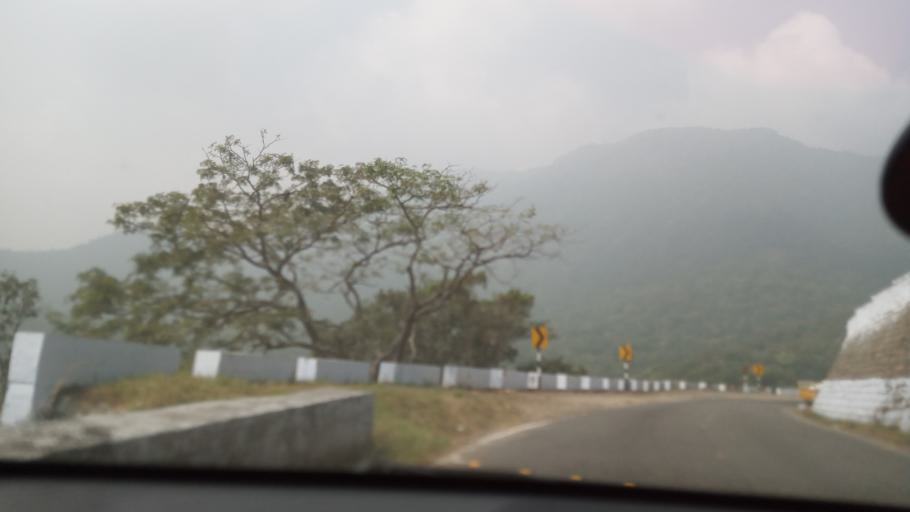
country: IN
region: Tamil Nadu
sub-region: Erode
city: Sathyamangalam
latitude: 11.5910
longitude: 77.1270
